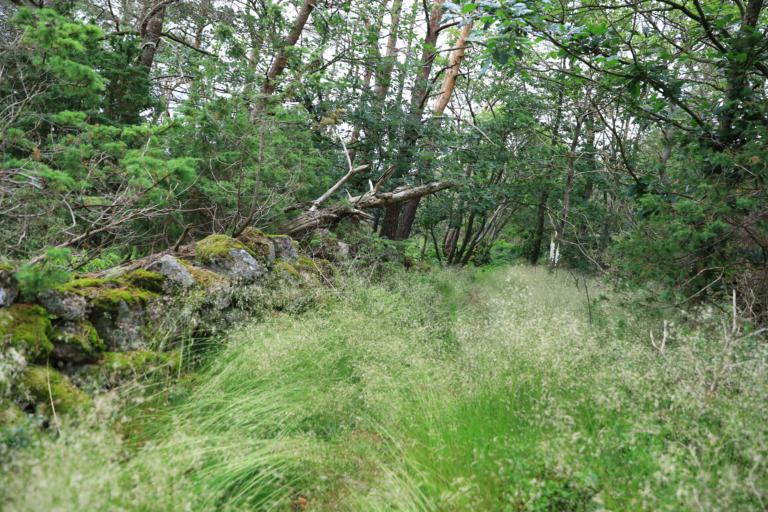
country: SE
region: Halland
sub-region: Varbergs Kommun
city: Varberg
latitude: 57.1719
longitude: 12.2854
